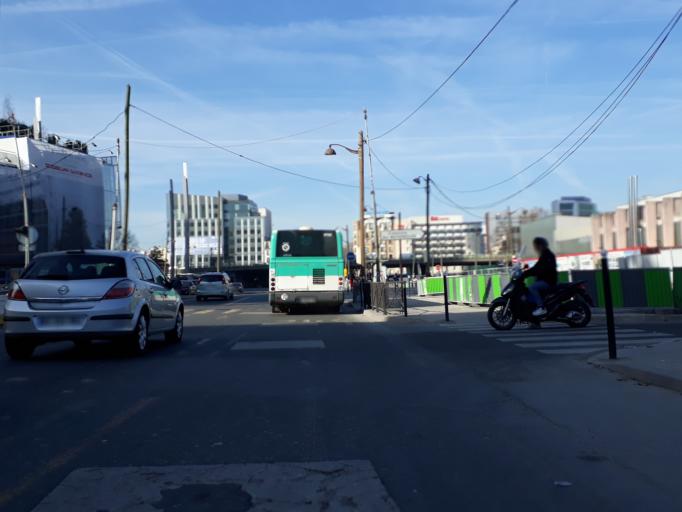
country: FR
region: Ile-de-France
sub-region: Departement des Hauts-de-Seine
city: Clichy
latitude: 48.8952
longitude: 2.3122
